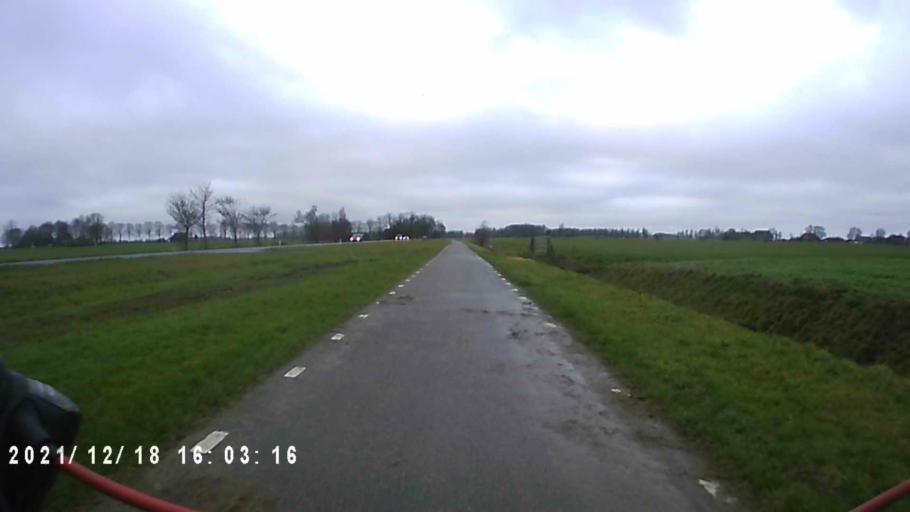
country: NL
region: Friesland
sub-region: Gemeente Dongeradeel
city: Anjum
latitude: 53.3493
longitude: 6.0813
